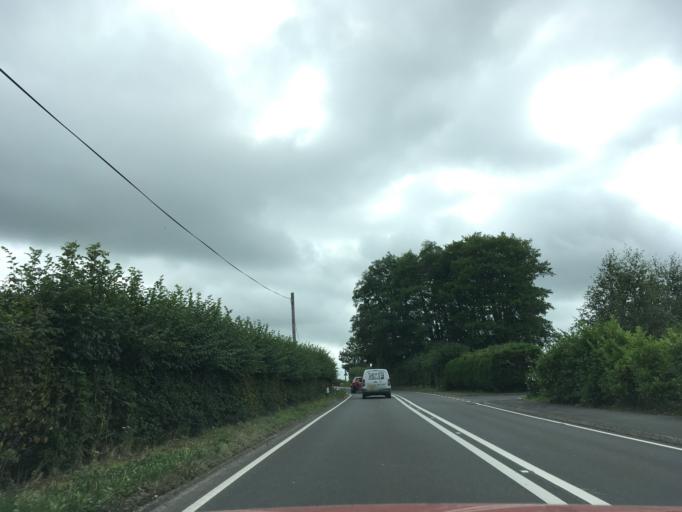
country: GB
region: Wales
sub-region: Carmarthenshire
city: Llanfynydd
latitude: 51.8755
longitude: -4.1129
